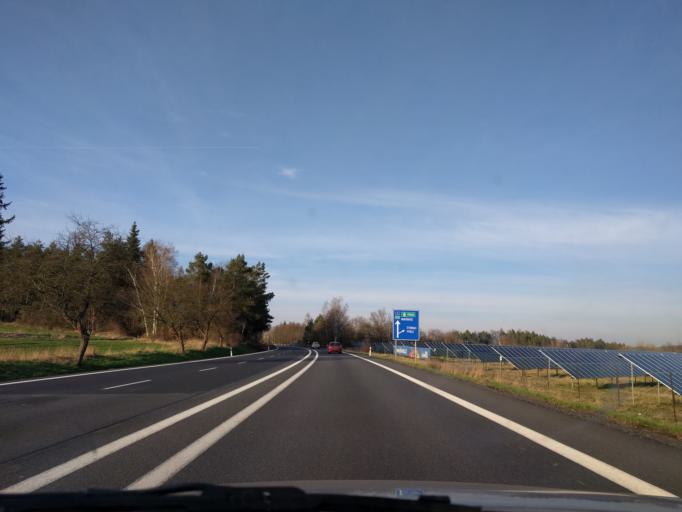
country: CZ
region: Central Bohemia
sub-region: Okres Benesov
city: Cercany
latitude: 49.8669
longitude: 14.7053
